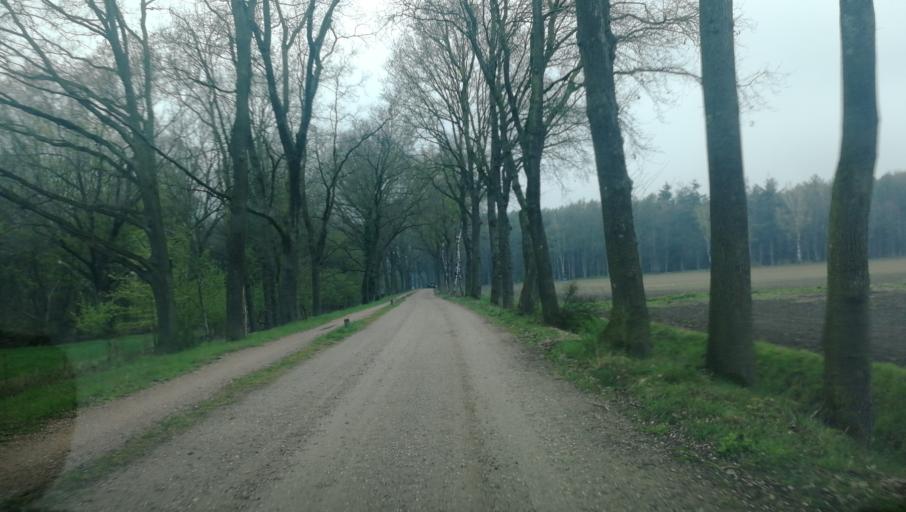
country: NL
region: Limburg
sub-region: Gemeente Beesel
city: Beesel
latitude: 51.2933
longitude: 6.0041
